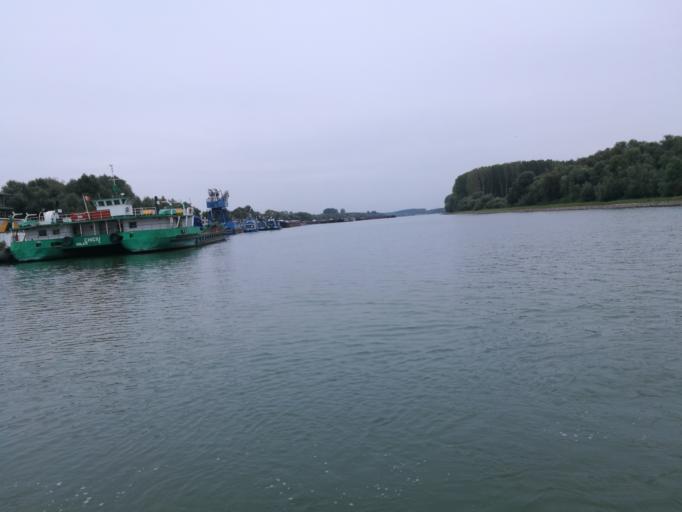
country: RO
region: Braila
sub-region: Municipiul Braila
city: Braila
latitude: 45.2859
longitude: 27.9966
